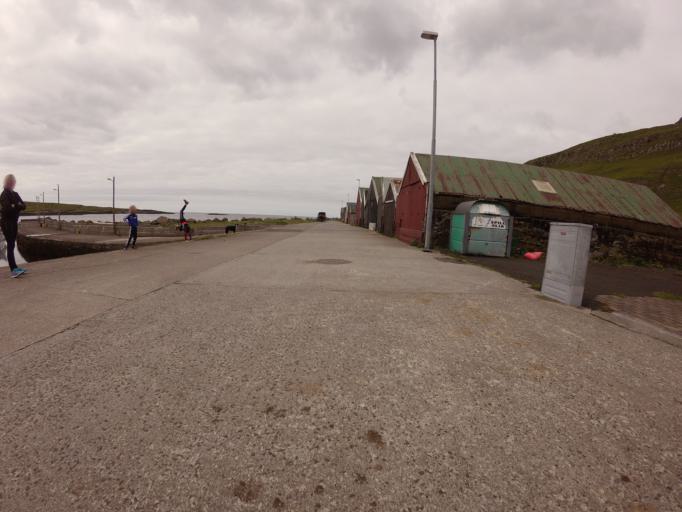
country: FO
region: Suduroy
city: Tvoroyri
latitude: 61.5258
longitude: -6.8814
